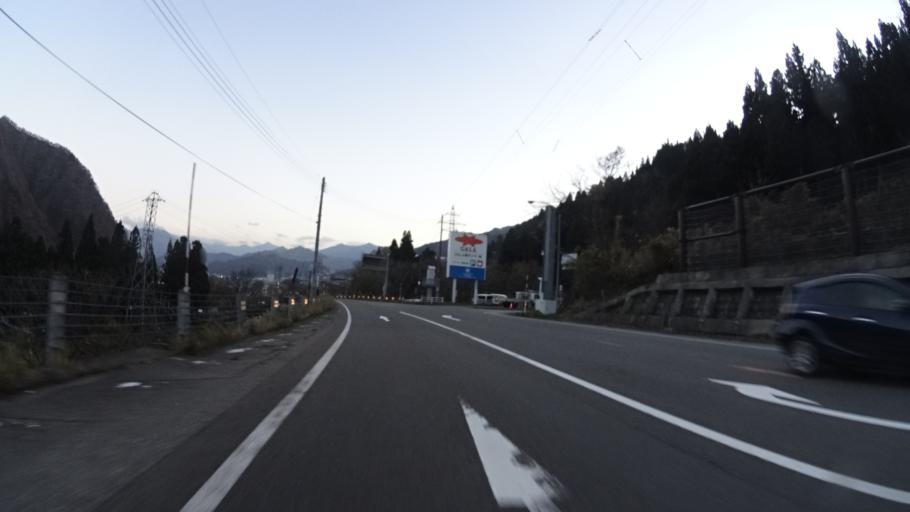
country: JP
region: Niigata
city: Shiozawa
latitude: 36.9554
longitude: 138.7992
